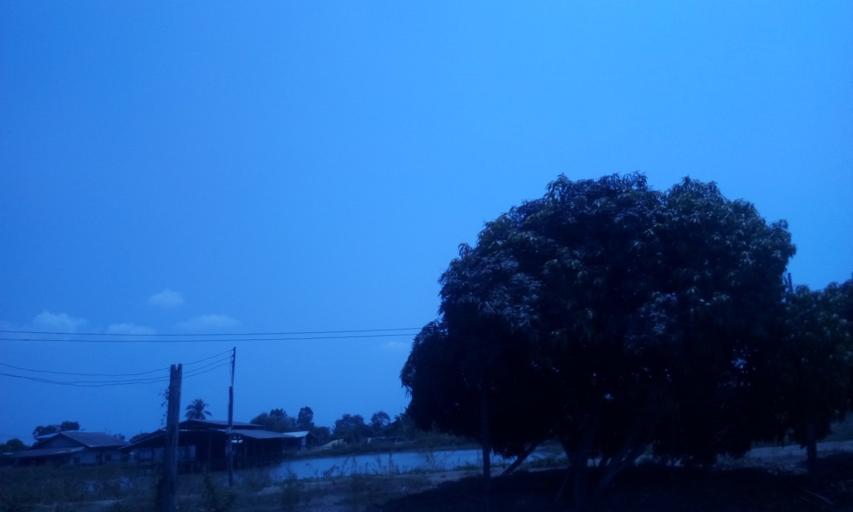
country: TH
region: Chachoengsao
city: Bang Nam Priao
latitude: 13.8533
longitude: 100.9653
